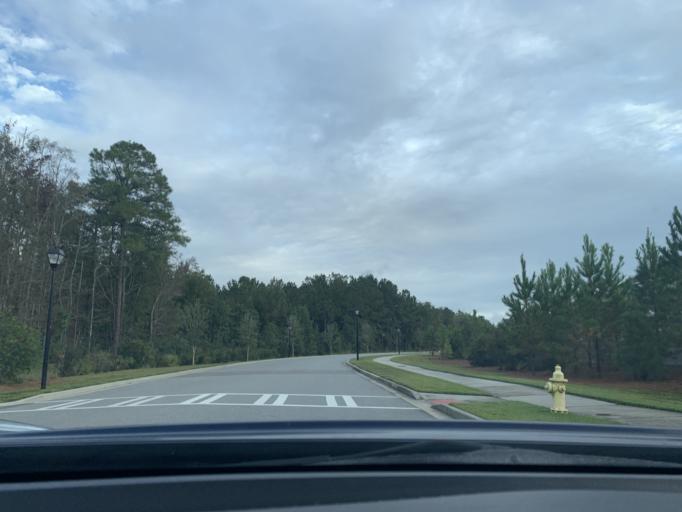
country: US
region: Georgia
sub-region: Chatham County
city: Pooler
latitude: 32.0740
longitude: -81.2593
